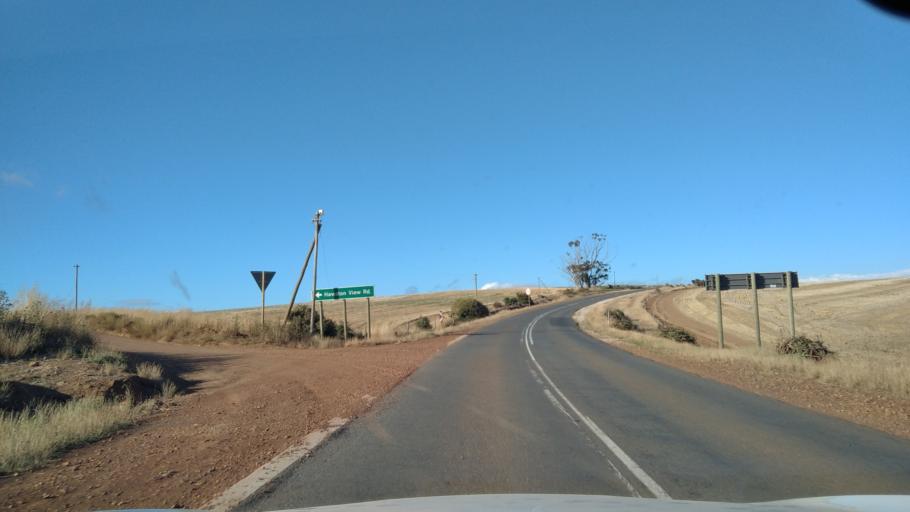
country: ZA
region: Western Cape
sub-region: Overberg District Municipality
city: Caledon
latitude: -34.1886
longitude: 19.2705
